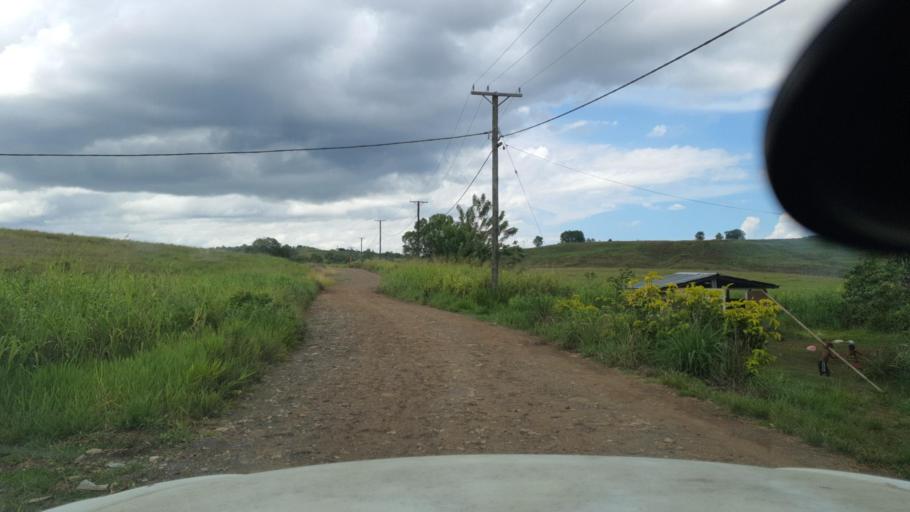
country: SB
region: Guadalcanal
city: Honiara
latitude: -9.5018
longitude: 160.1129
